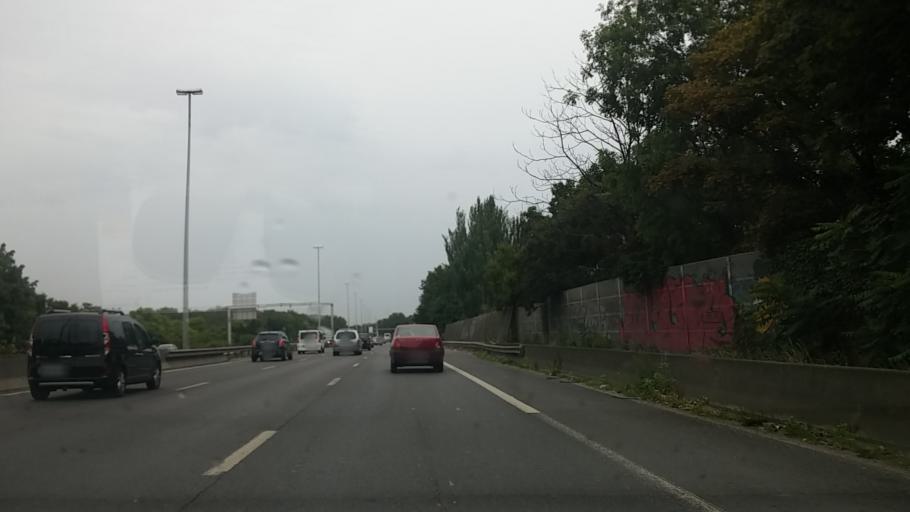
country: FR
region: Ile-de-France
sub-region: Departement de Seine-Saint-Denis
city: La Courneuve
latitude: 48.9338
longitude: 2.3855
